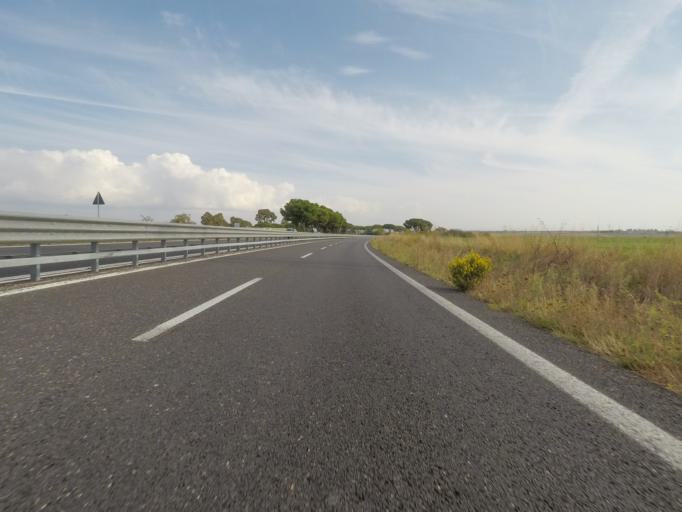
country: IT
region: Latium
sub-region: Provincia di Viterbo
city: Pescia Romana
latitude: 42.3910
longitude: 11.5393
